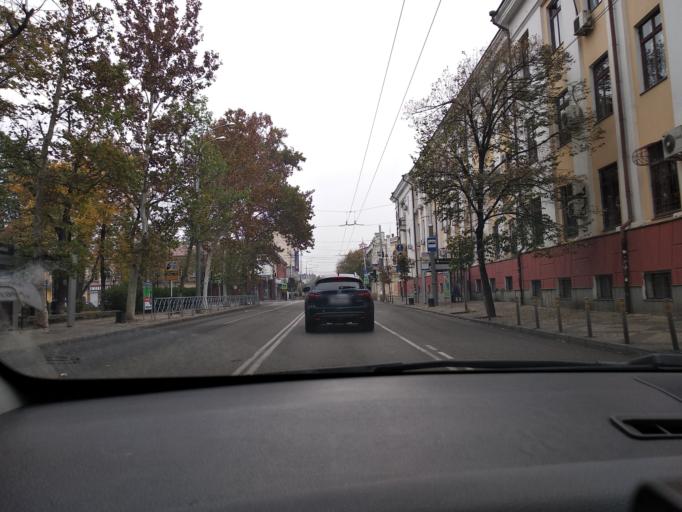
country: RU
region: Krasnodarskiy
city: Krasnodar
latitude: 45.0213
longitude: 38.9660
